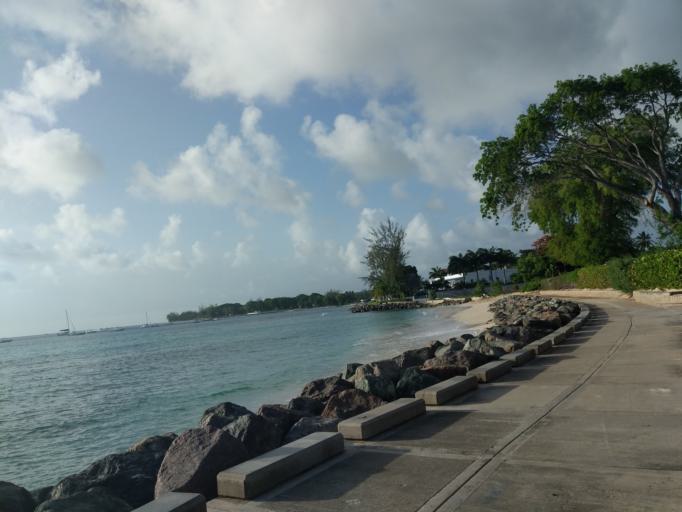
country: BB
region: Saint James
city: Holetown
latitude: 13.1813
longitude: -59.6395
